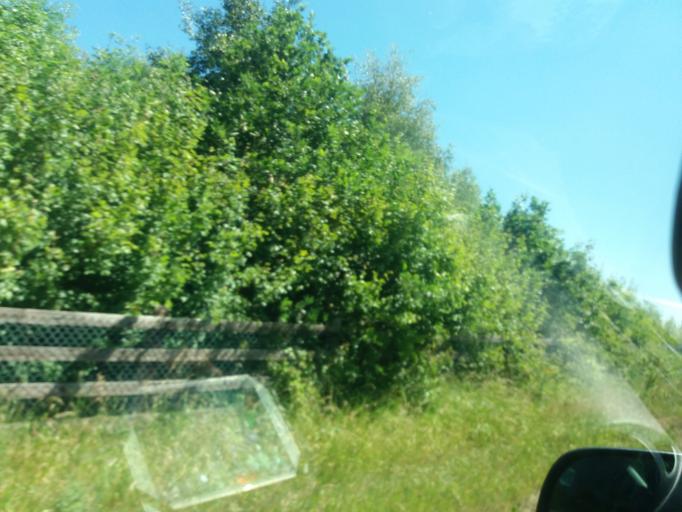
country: IE
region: Leinster
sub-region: Fingal County
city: Swords
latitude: 53.4770
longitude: -6.2719
